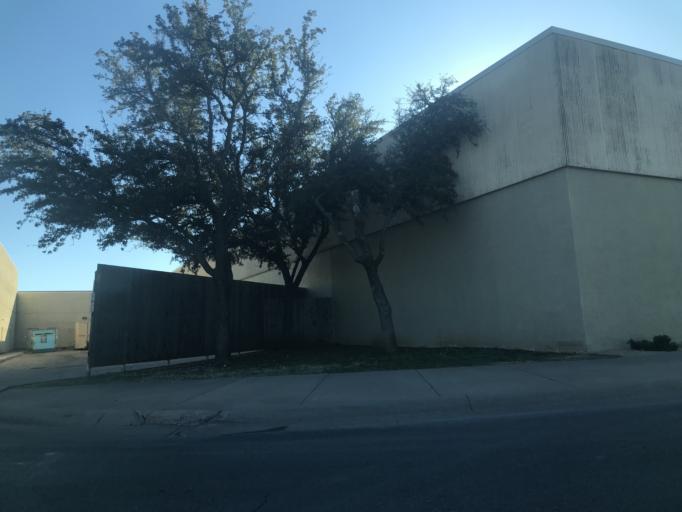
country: US
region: Texas
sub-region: Tom Green County
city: San Angelo
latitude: 31.4285
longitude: -100.4986
